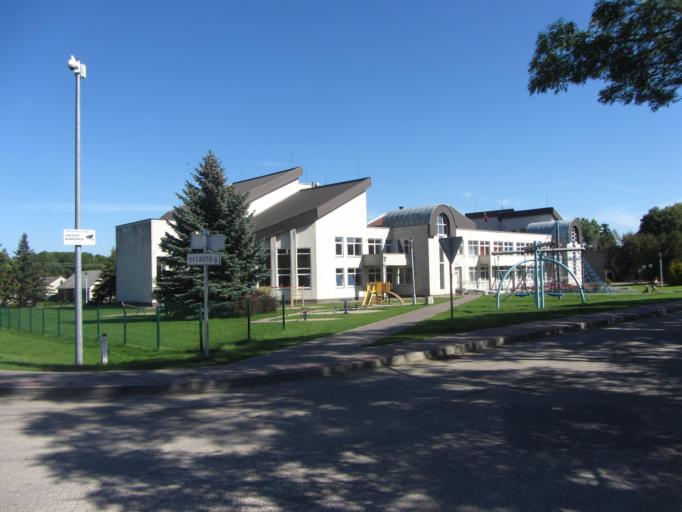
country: LT
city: Simnas
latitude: 54.4361
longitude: 23.7636
